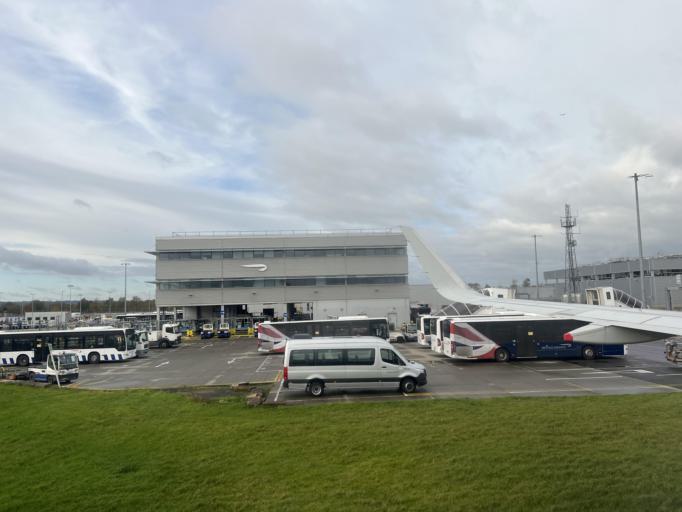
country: GB
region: England
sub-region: Buckinghamshire
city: Iver
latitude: 51.4677
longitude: -0.4876
